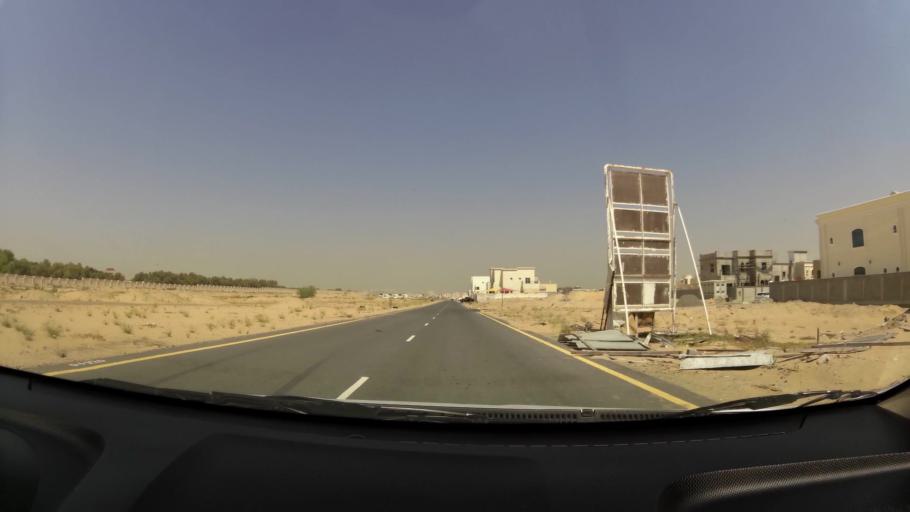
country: AE
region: Ajman
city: Ajman
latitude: 25.4029
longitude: 55.5370
